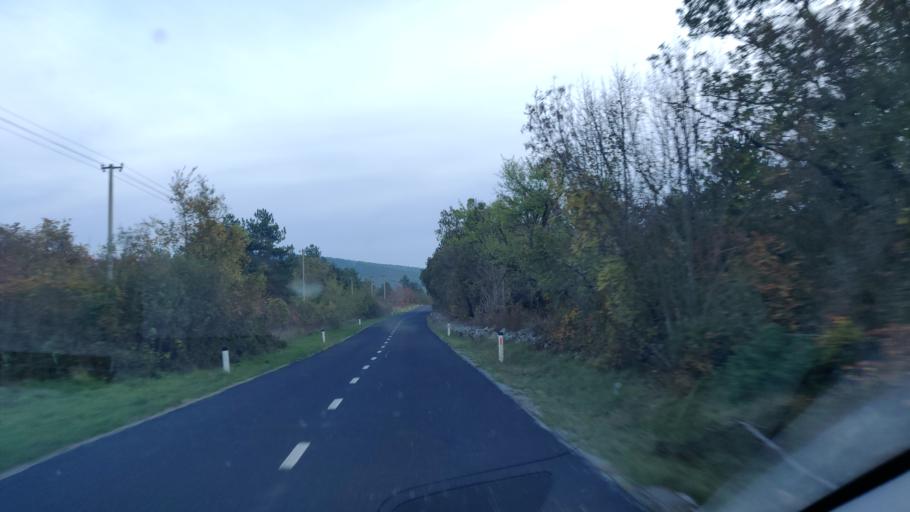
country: SI
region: Sezana
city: Sezana
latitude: 45.7455
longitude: 13.9273
